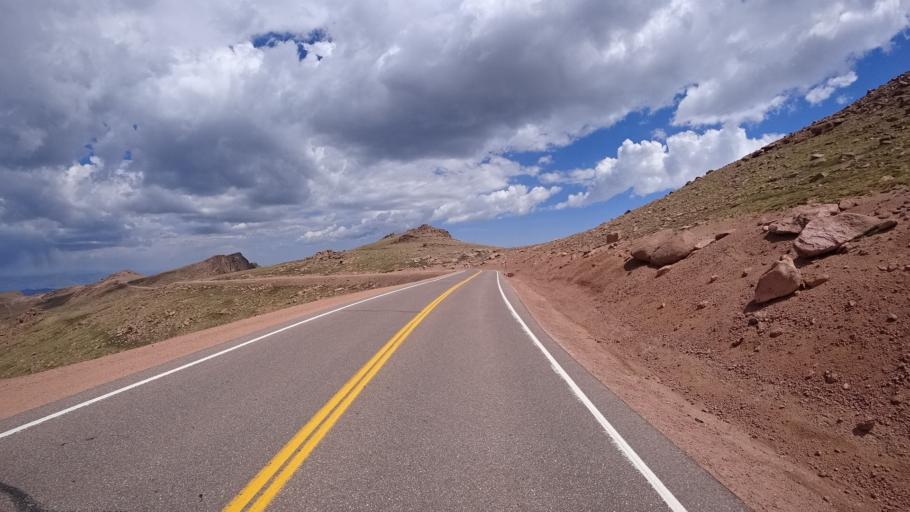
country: US
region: Colorado
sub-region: El Paso County
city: Cascade-Chipita Park
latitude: 38.8499
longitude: -105.0620
